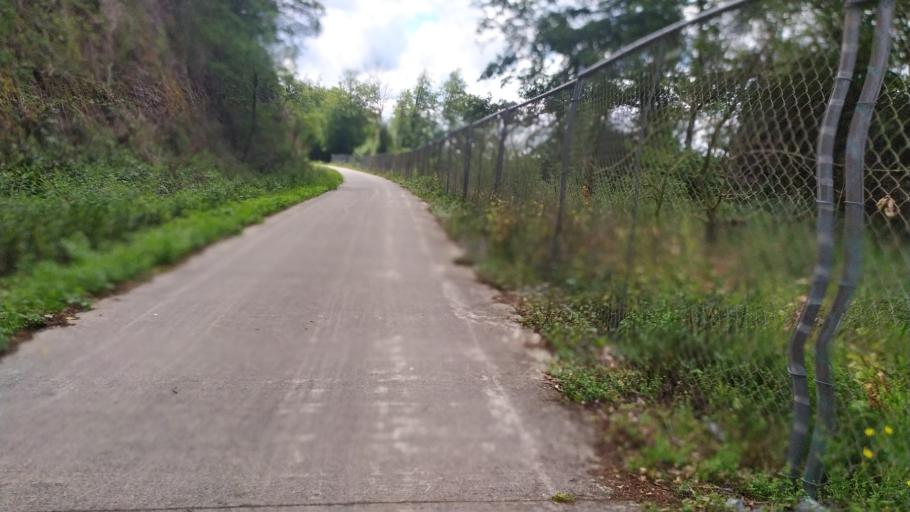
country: BE
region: Wallonia
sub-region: Province du Luxembourg
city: Wellin
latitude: 50.1584
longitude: 5.1173
